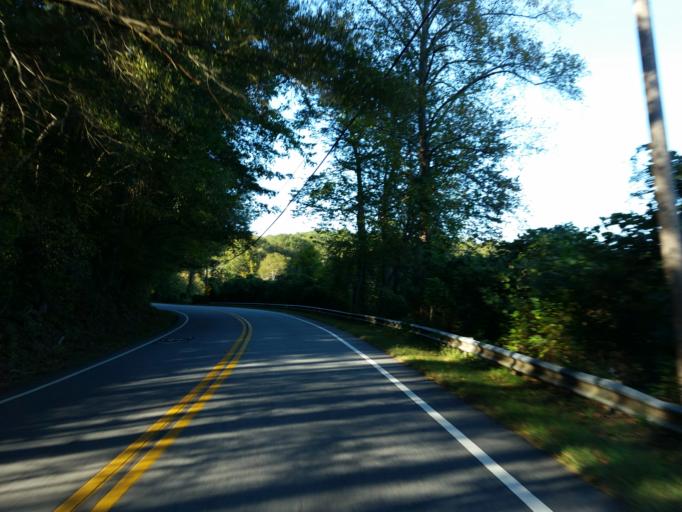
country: US
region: Georgia
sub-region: Fulton County
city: Roswell
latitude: 33.9980
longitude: -84.3844
